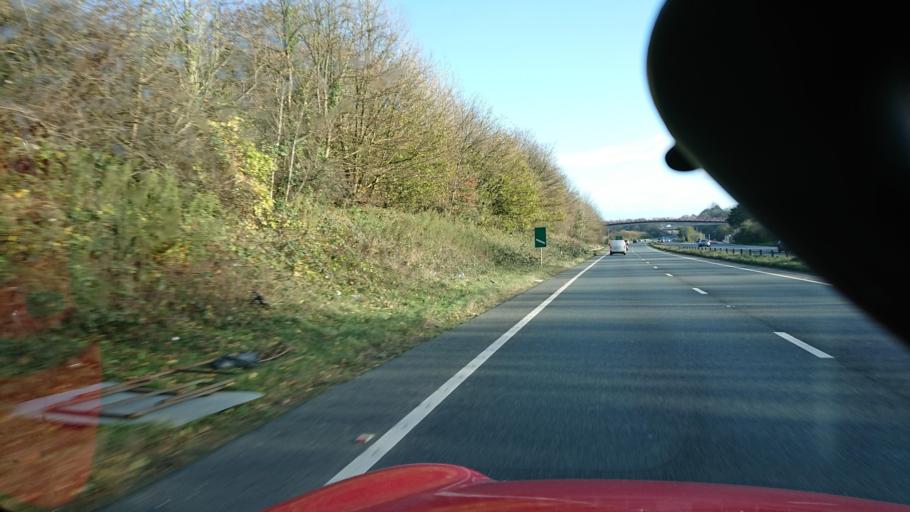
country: GB
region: England
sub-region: Cornwall
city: Torpoint
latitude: 50.4095
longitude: -4.1689
